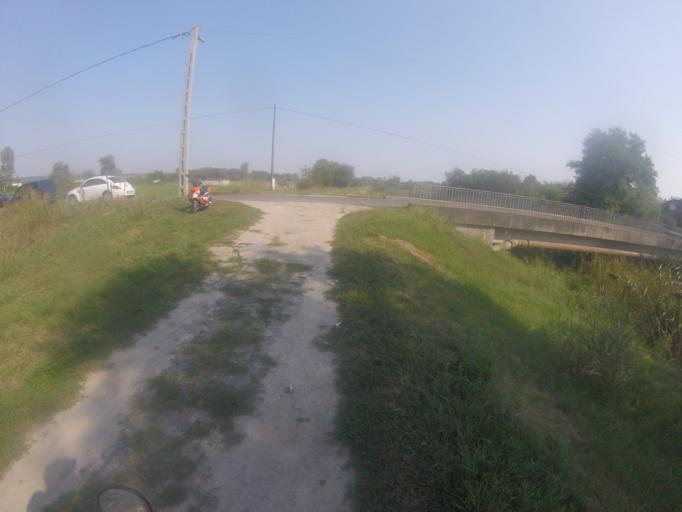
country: HU
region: Bacs-Kiskun
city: Baja
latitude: 46.2036
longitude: 18.9546
